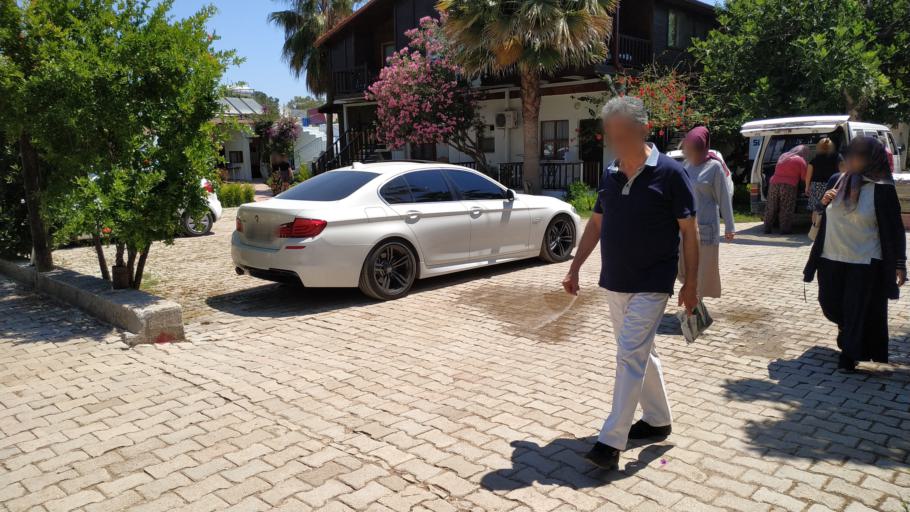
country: TR
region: Antalya
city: Tekirova
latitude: 36.4061
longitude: 30.4766
